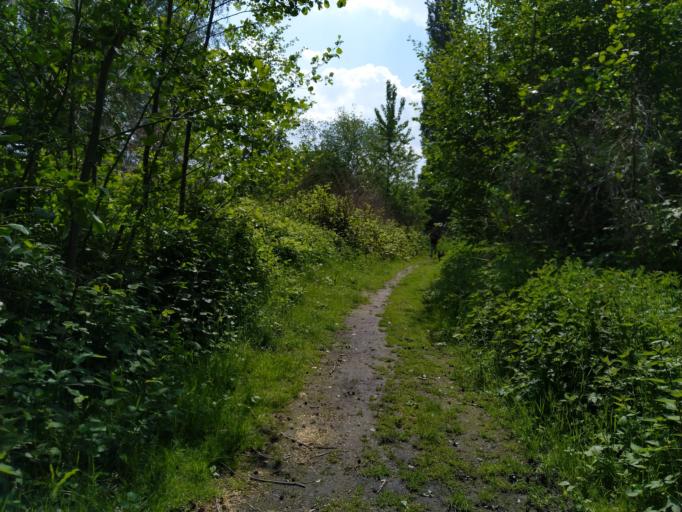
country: BE
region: Wallonia
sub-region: Province du Hainaut
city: Roeulx
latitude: 50.4686
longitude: 4.0472
